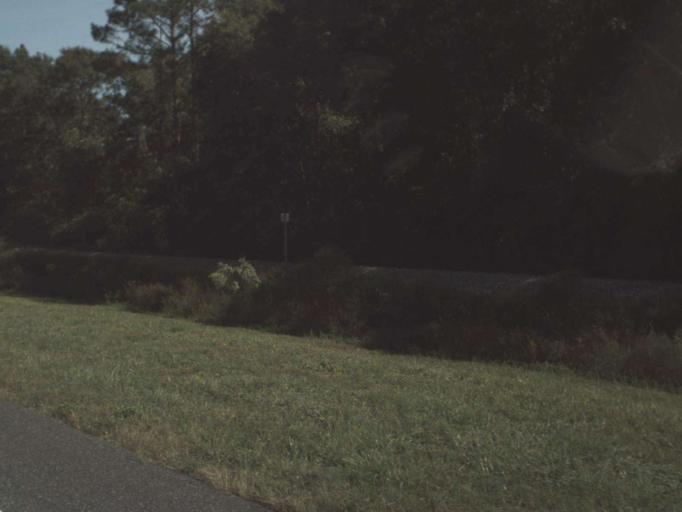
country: US
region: Florida
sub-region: Bay County
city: Youngstown
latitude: 30.4452
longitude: -85.4258
